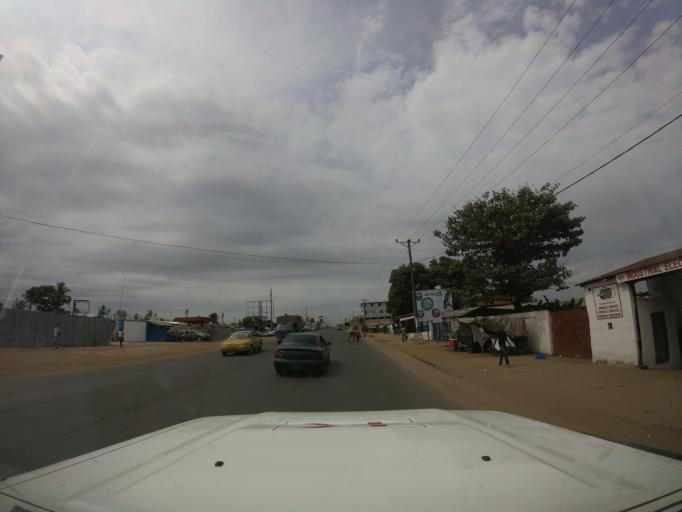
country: LR
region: Montserrado
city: Monrovia
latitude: 6.3634
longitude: -10.7869
